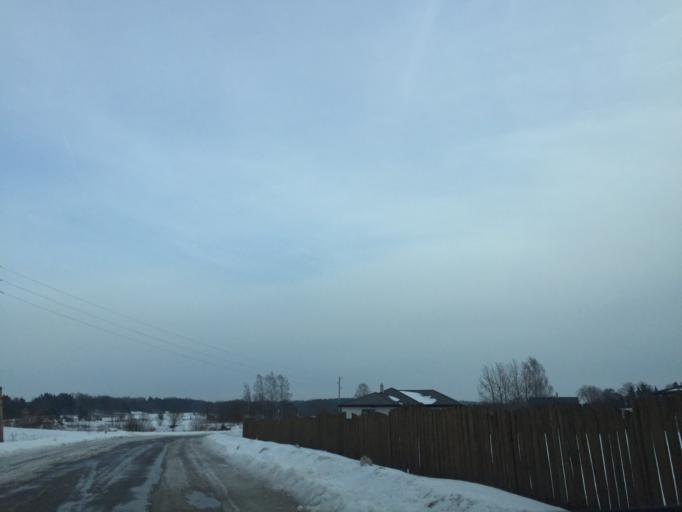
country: LV
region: Ikskile
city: Ikskile
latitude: 56.8450
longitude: 24.4578
